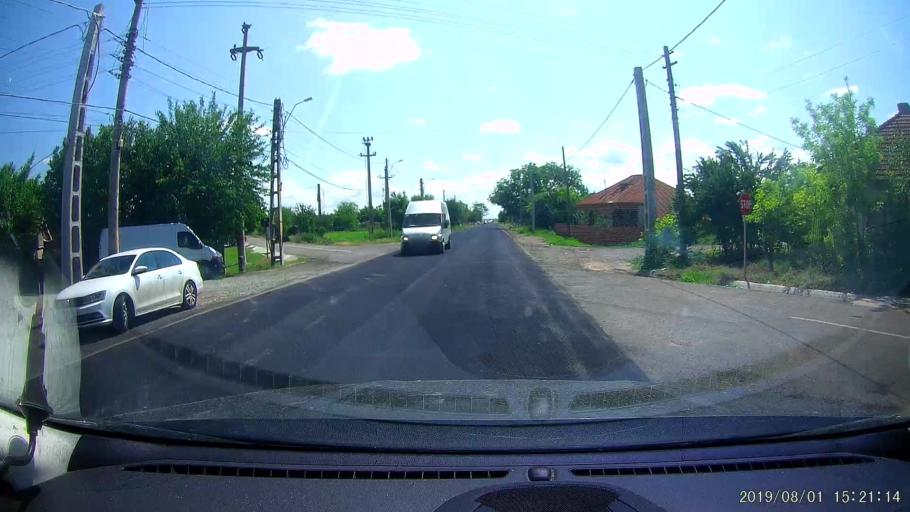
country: RO
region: Braila
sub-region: Comuna Tufesti
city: Tufesti
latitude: 45.0721
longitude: 27.7987
